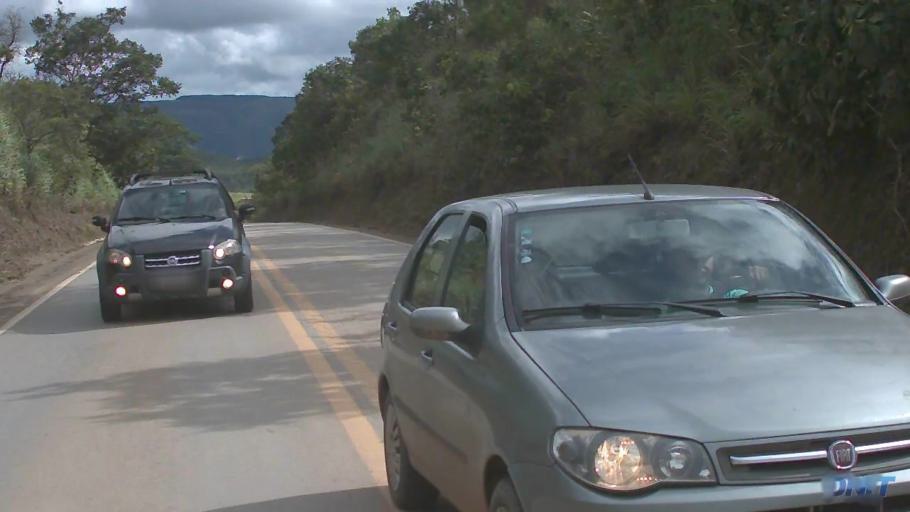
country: BR
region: Goias
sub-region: Padre Bernardo
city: Padre Bernardo
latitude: -15.4755
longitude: -48.2317
